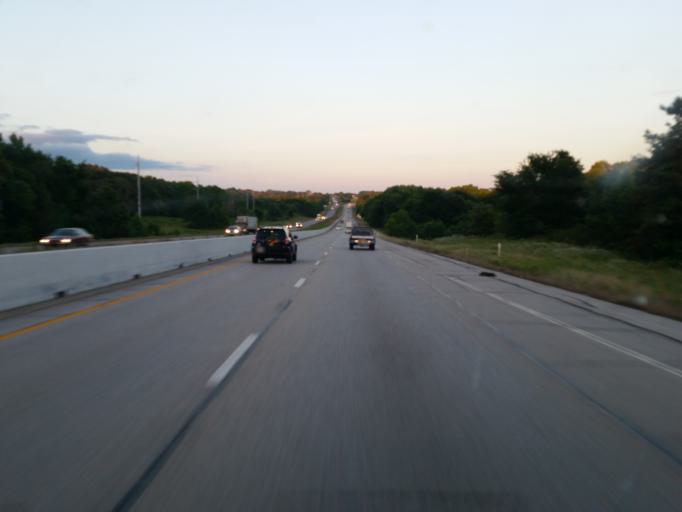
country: US
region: Texas
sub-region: Smith County
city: Hideaway
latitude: 32.4828
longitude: -95.5168
